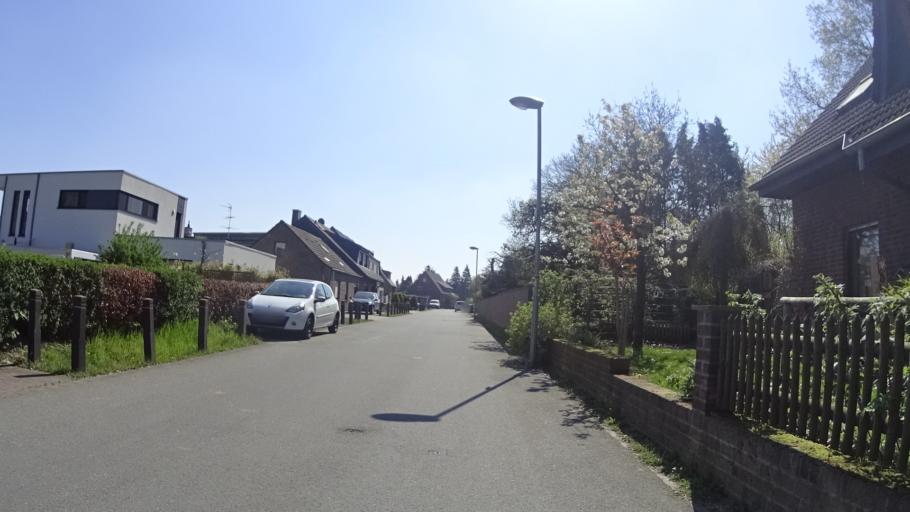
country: DE
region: North Rhine-Westphalia
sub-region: Regierungsbezirk Dusseldorf
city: Moers
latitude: 51.4234
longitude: 6.6177
